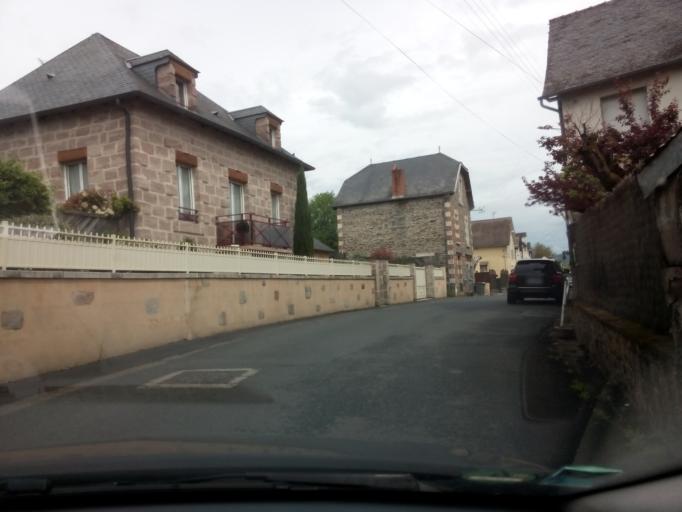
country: FR
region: Limousin
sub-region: Departement de la Correze
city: Objat
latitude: 45.2594
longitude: 1.4058
